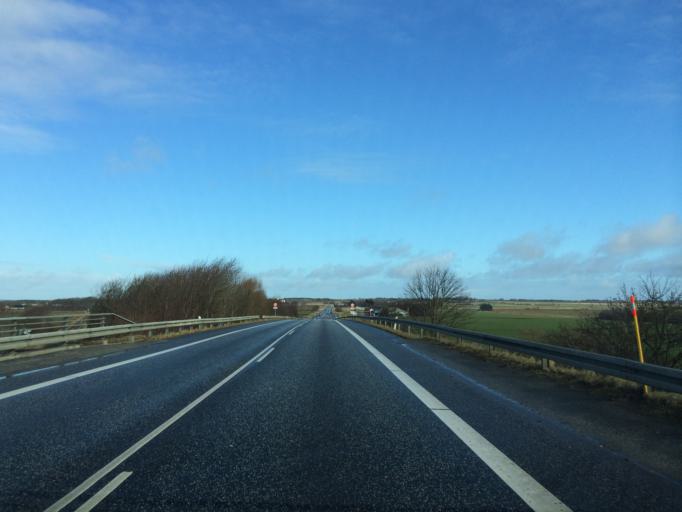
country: DK
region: Central Jutland
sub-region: Holstebro Kommune
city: Ulfborg
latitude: 56.2794
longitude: 8.3271
